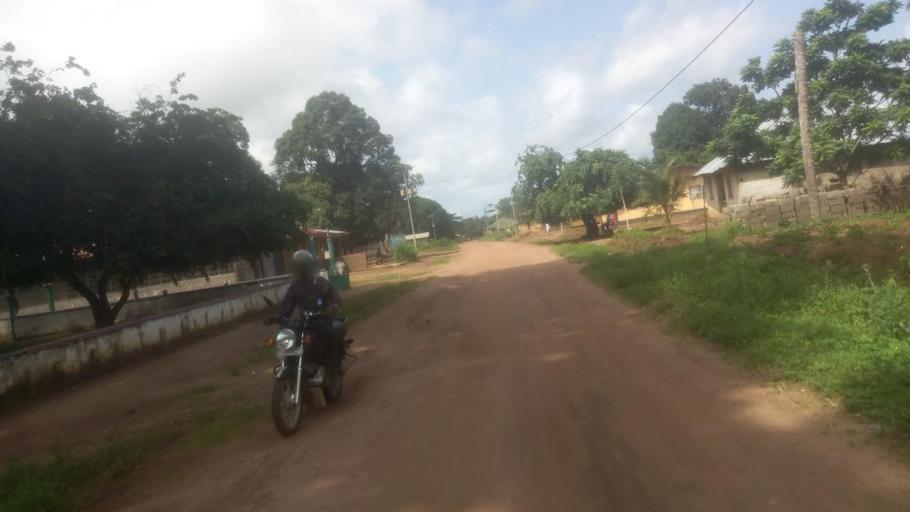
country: SL
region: Northern Province
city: Tintafor
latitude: 8.6397
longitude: -13.2235
